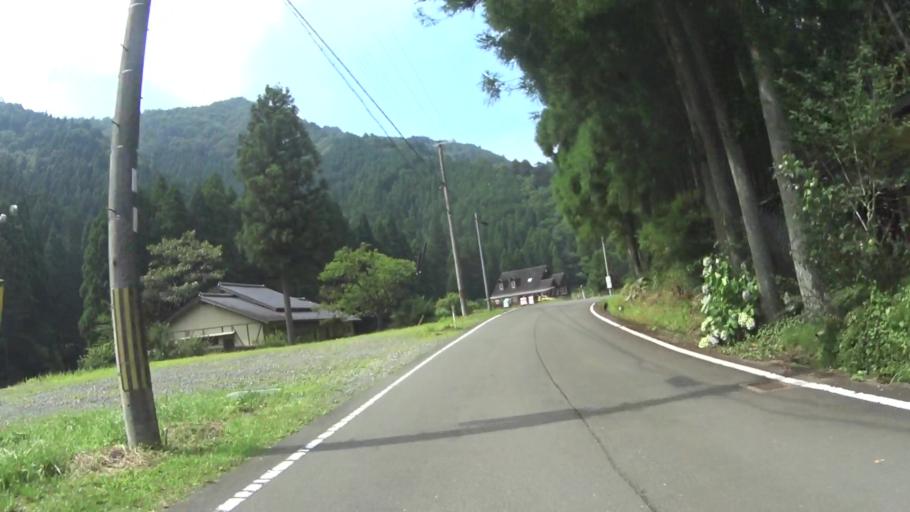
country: JP
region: Fukui
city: Obama
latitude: 35.3252
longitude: 135.6443
